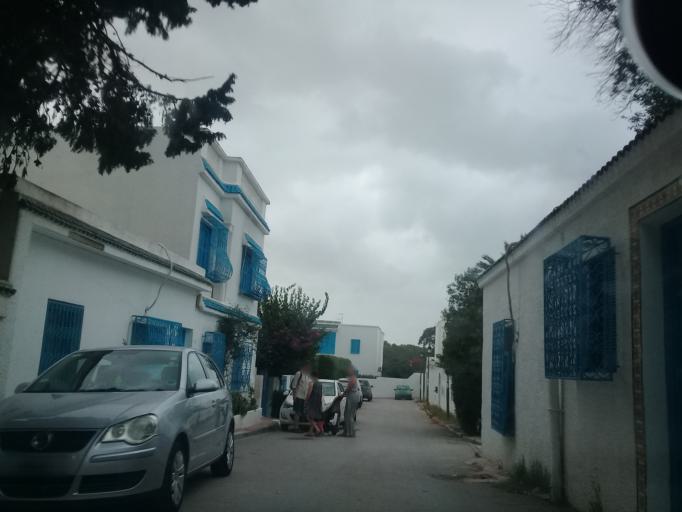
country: TN
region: Tunis
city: Sidi Bou Said
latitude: 36.8729
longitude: 10.3417
